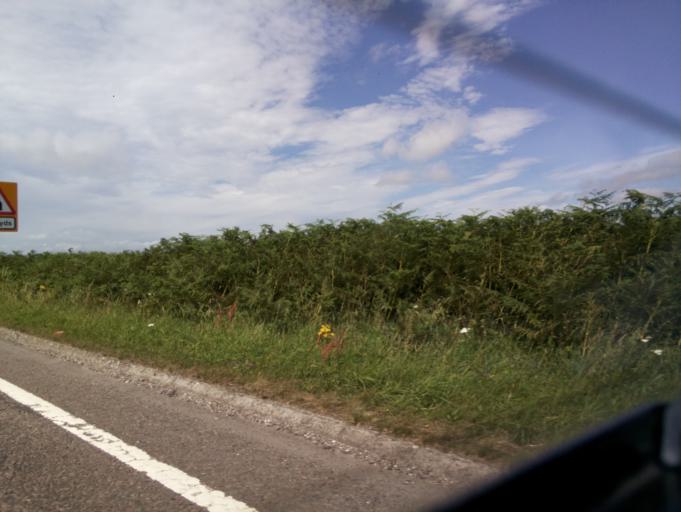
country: GB
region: England
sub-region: Dorset
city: Dorchester
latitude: 50.7945
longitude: -2.5482
